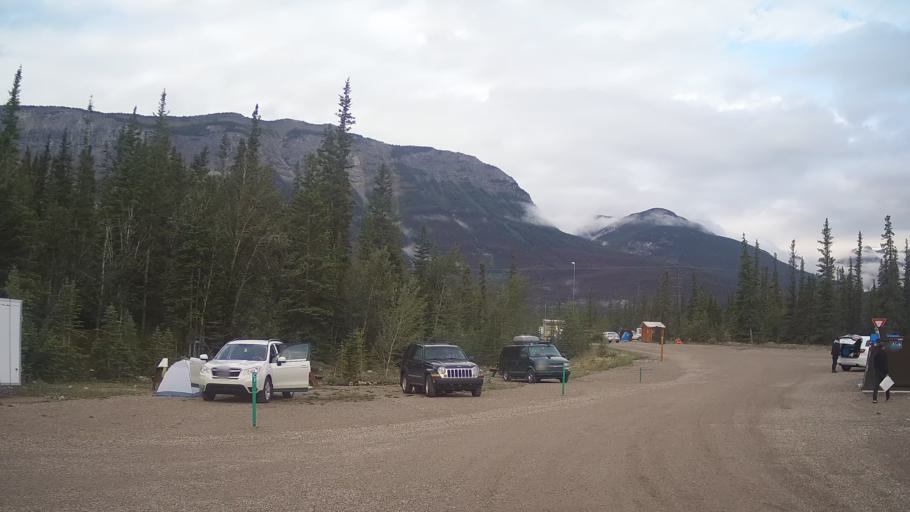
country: CA
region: Alberta
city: Jasper Park Lodge
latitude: 53.0152
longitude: -118.0845
